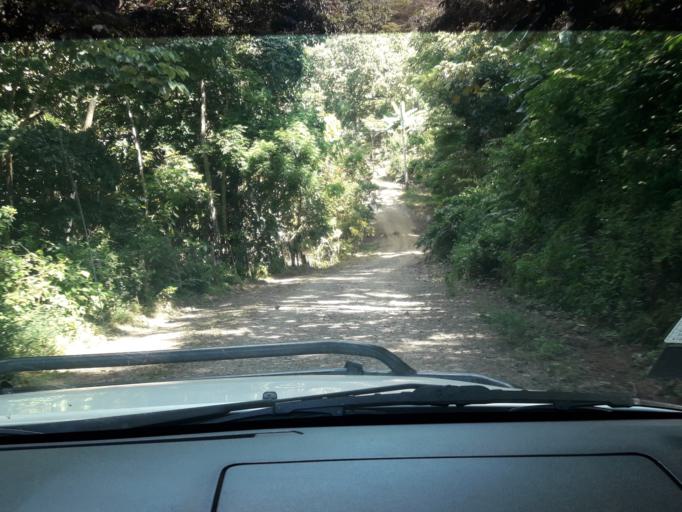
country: CR
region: Guanacaste
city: La Cruz
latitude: 11.1812
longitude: -85.6625
